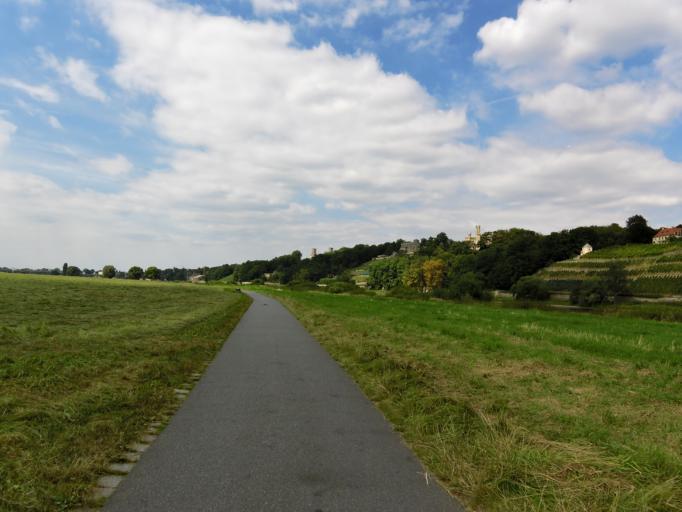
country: DE
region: Saxony
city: Albertstadt
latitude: 51.0590
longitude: 13.8031
